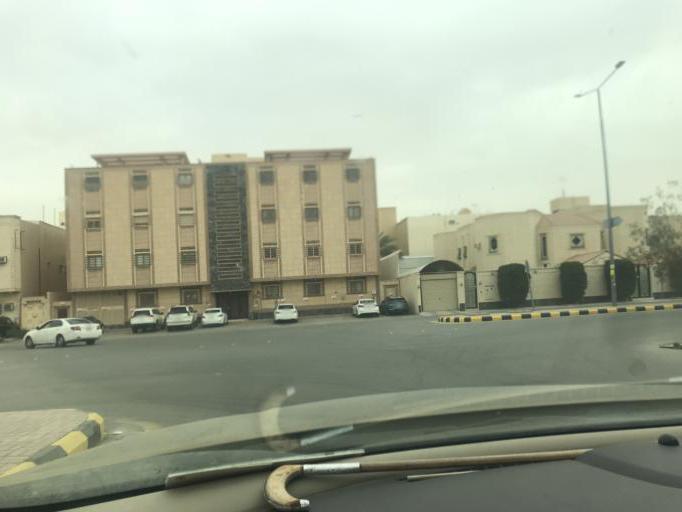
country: SA
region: Ar Riyad
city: Riyadh
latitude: 24.7373
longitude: 46.7550
